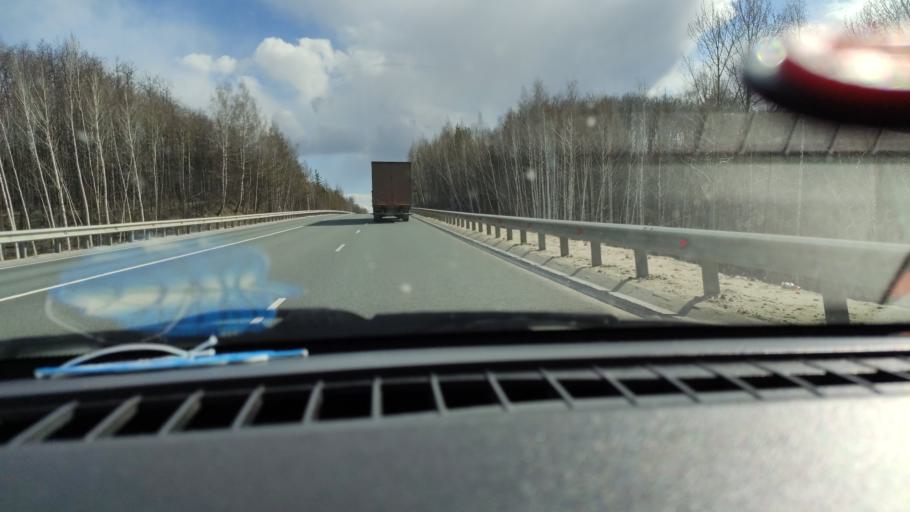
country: RU
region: Saratov
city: Khvalynsk
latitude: 52.4957
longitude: 48.0144
